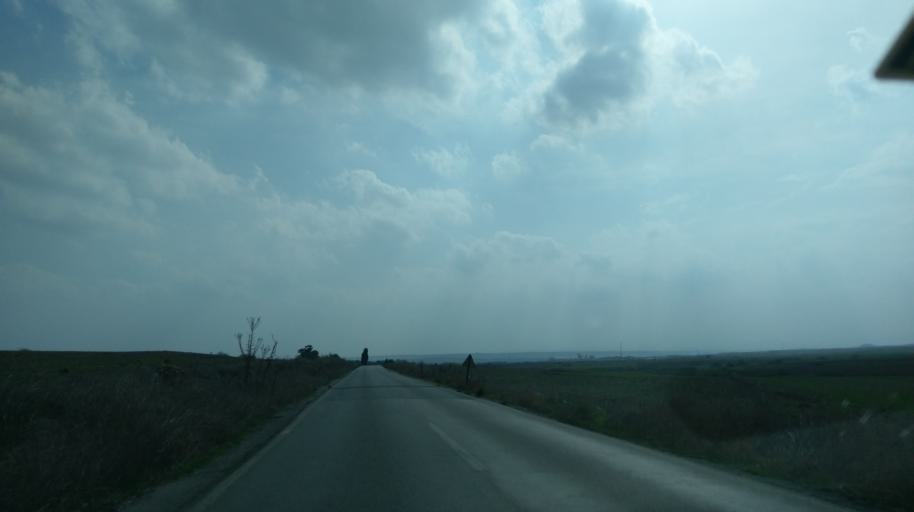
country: CY
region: Lefkosia
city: Mammari
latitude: 35.2448
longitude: 33.1546
